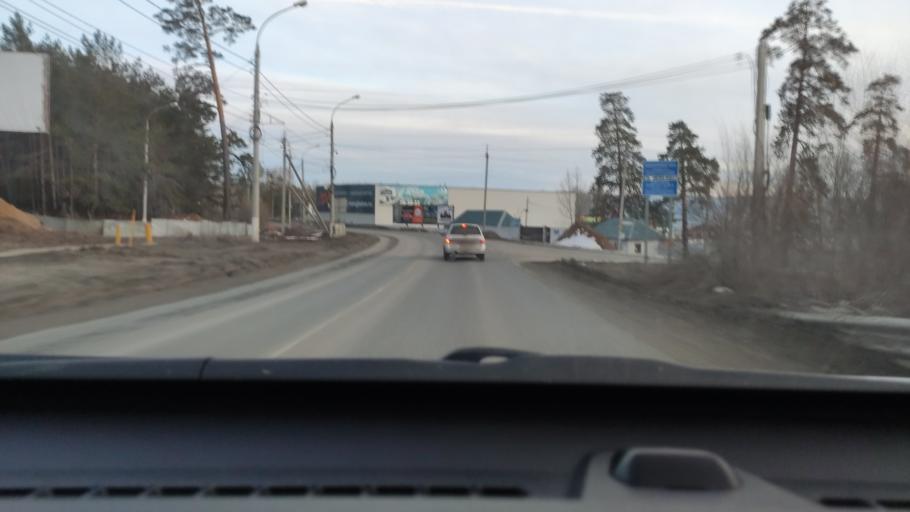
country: RU
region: Samara
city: Tol'yatti
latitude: 53.4782
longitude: 49.3266
